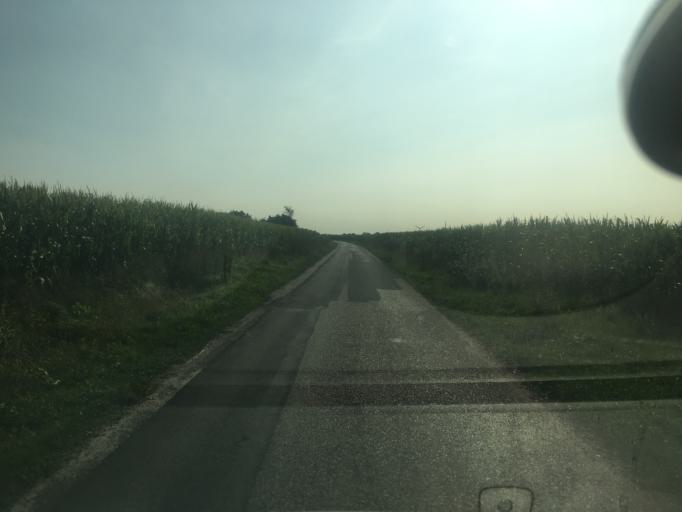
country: DK
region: South Denmark
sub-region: Tonder Kommune
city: Tonder
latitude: 54.9936
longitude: 8.9118
